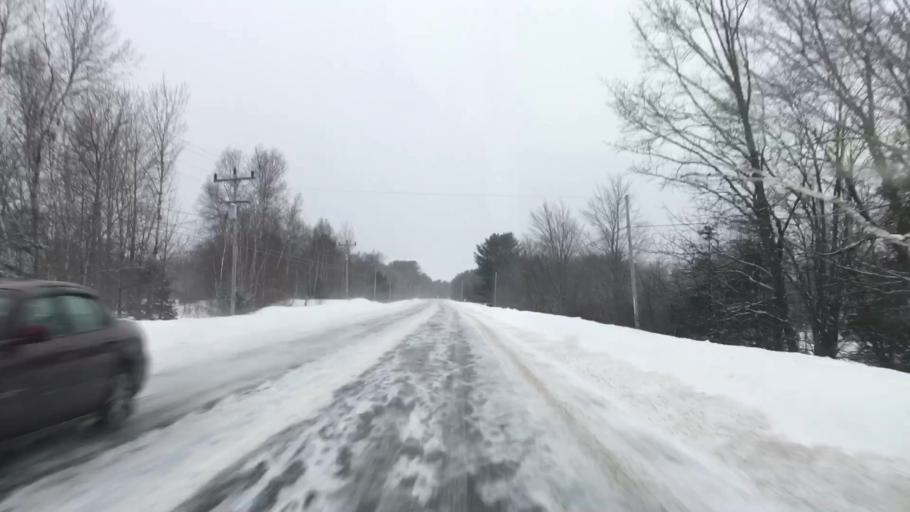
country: US
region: Maine
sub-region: Penobscot County
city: Medway
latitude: 45.5612
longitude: -68.3917
